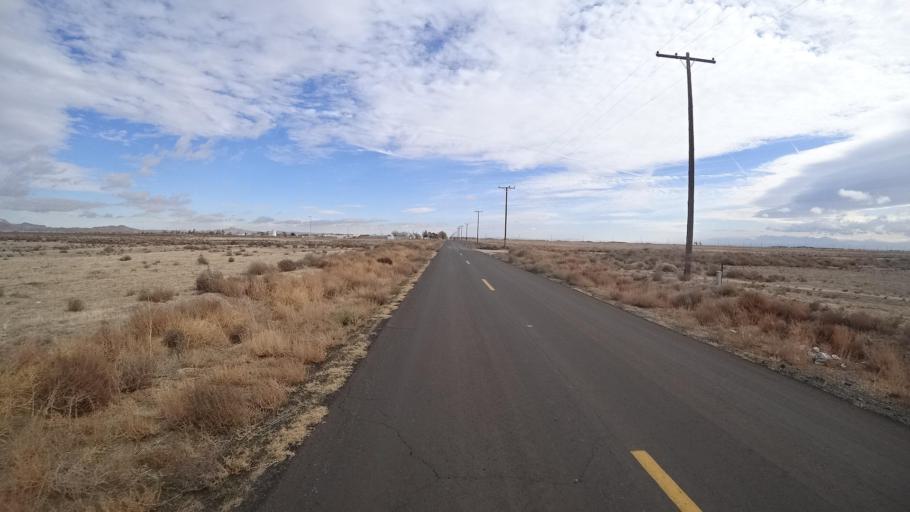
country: US
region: California
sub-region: Kern County
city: Rosamond
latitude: 34.8201
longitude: -118.2998
